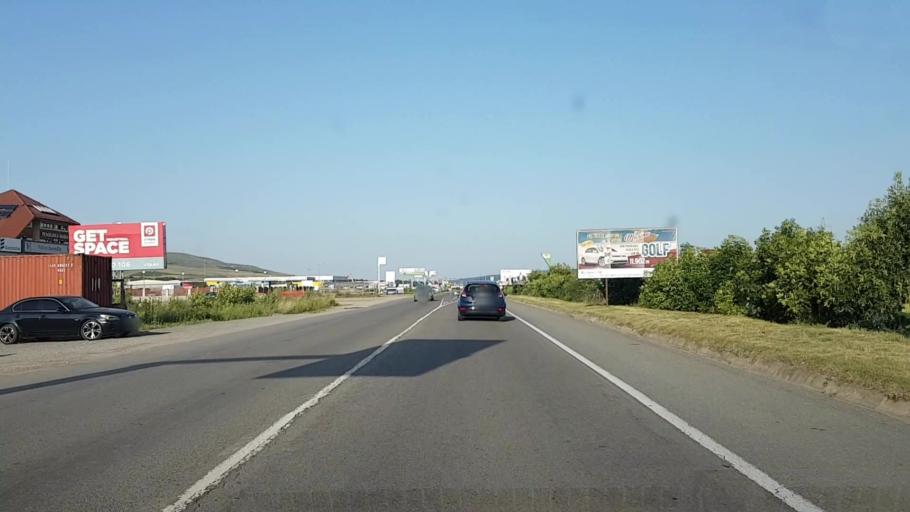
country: RO
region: Cluj
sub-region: Comuna Floresti
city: Luna de Sus
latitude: 46.7509
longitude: 23.4270
